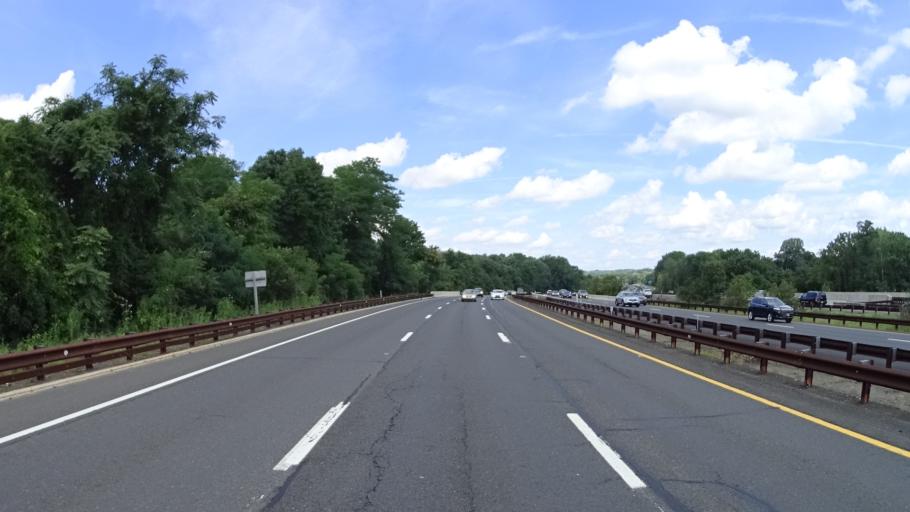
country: US
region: New Jersey
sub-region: Monmouth County
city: Lincroft
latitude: 40.3454
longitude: -74.1134
